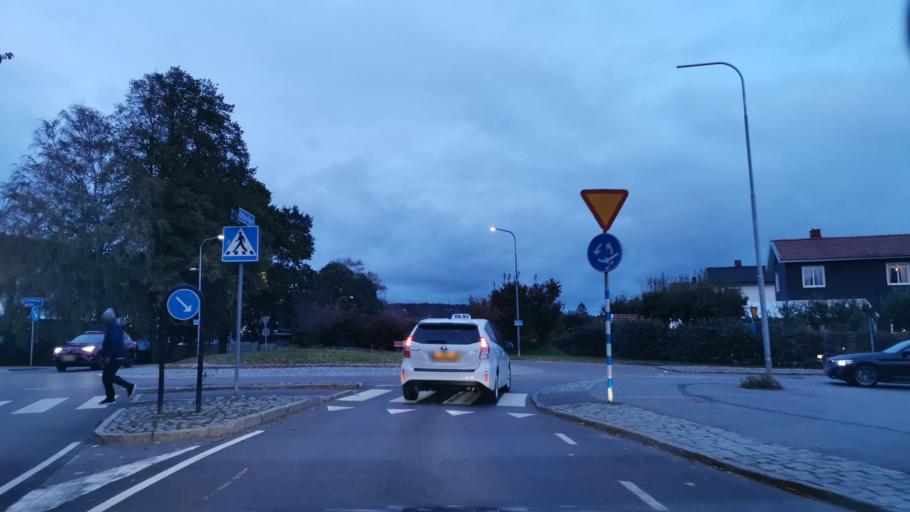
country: SE
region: Vaestra Goetaland
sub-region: Goteborg
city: Eriksbo
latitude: 57.7374
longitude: 12.0591
